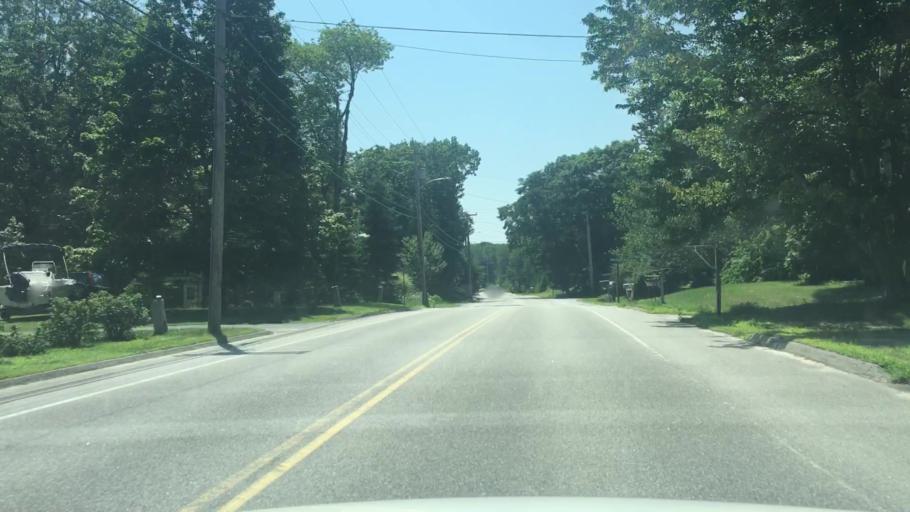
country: US
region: Maine
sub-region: Cumberland County
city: Falmouth
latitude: 43.7319
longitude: -70.2394
